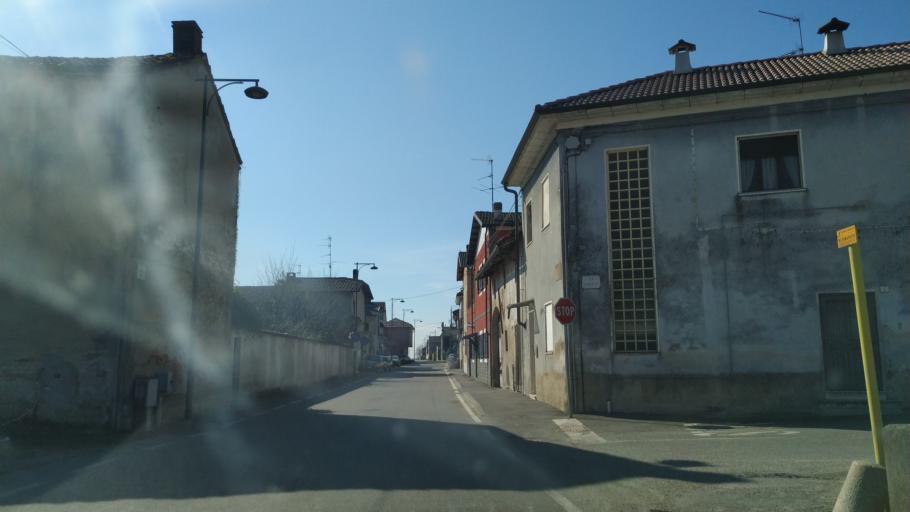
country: IT
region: Piedmont
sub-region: Provincia di Vercelli
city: Asigliano Vercellese
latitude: 45.2582
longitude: 8.4115
